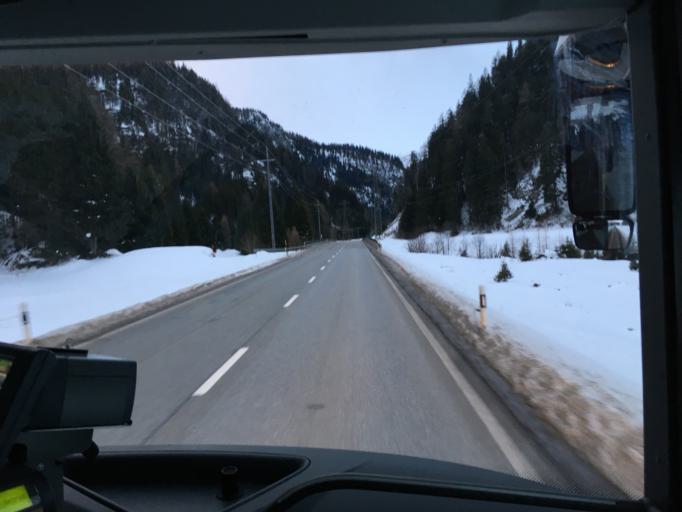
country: CH
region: Grisons
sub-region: Albula District
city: Tiefencastel
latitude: 46.5464
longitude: 9.6252
